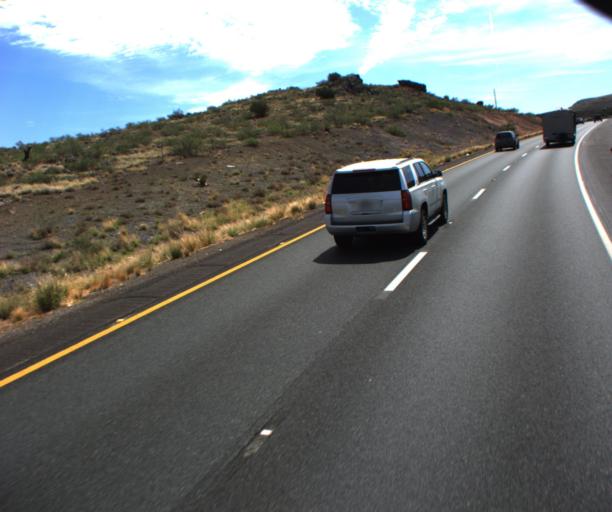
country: US
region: Arizona
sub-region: Yavapai County
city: Cordes Lakes
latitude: 34.4218
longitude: -112.0573
